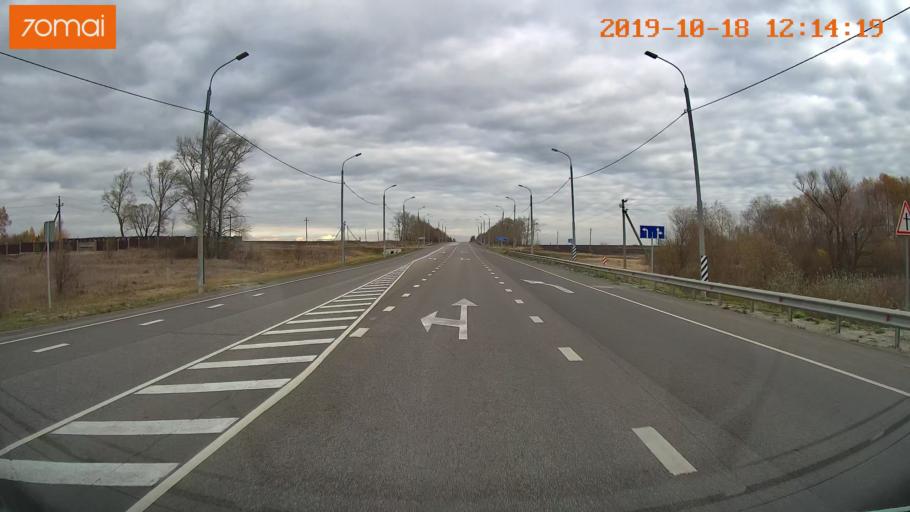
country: RU
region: Rjazan
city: Zakharovo
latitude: 54.4293
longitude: 39.3812
